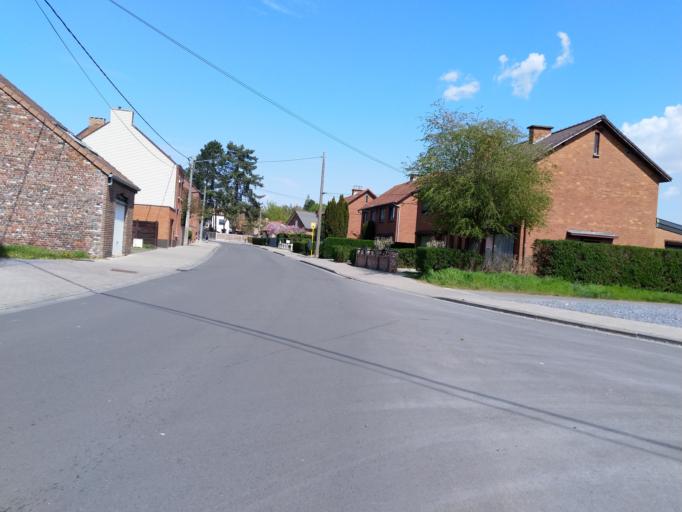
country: BE
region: Wallonia
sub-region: Province du Hainaut
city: Mons
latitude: 50.4738
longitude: 3.9224
